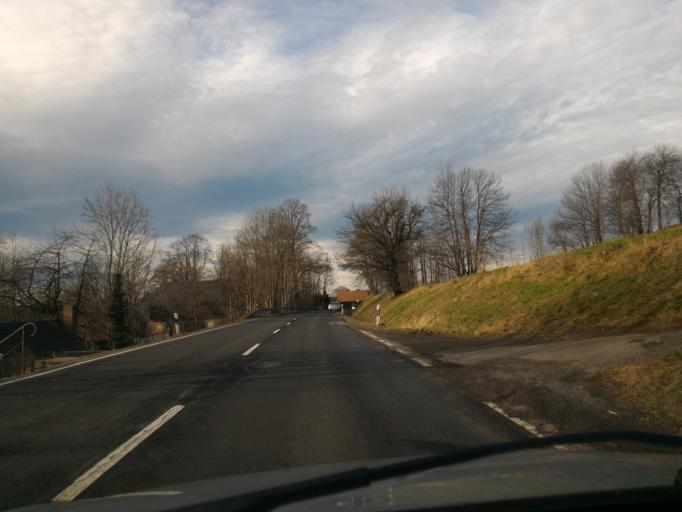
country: DE
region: Saxony
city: Demitz-Thumitz
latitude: 51.0995
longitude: 14.2516
